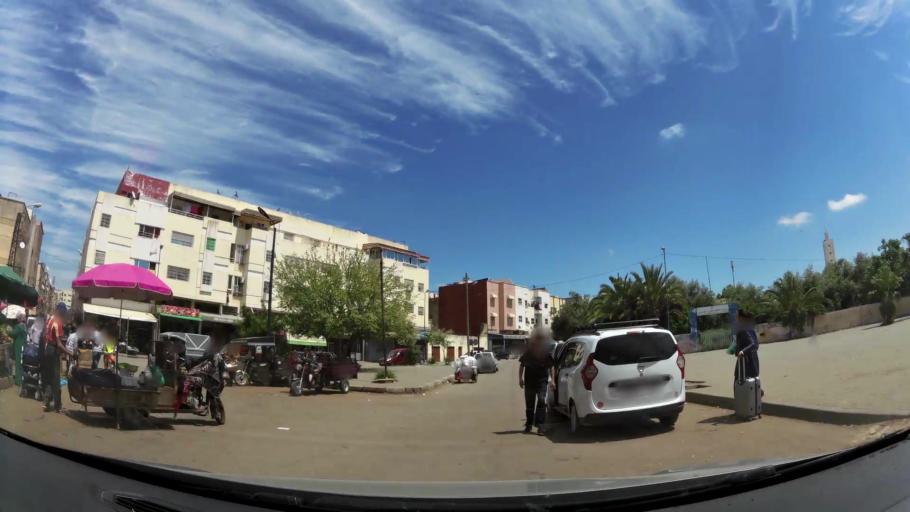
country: MA
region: Fes-Boulemane
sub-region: Fes
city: Fes
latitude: 34.0125
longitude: -4.9850
